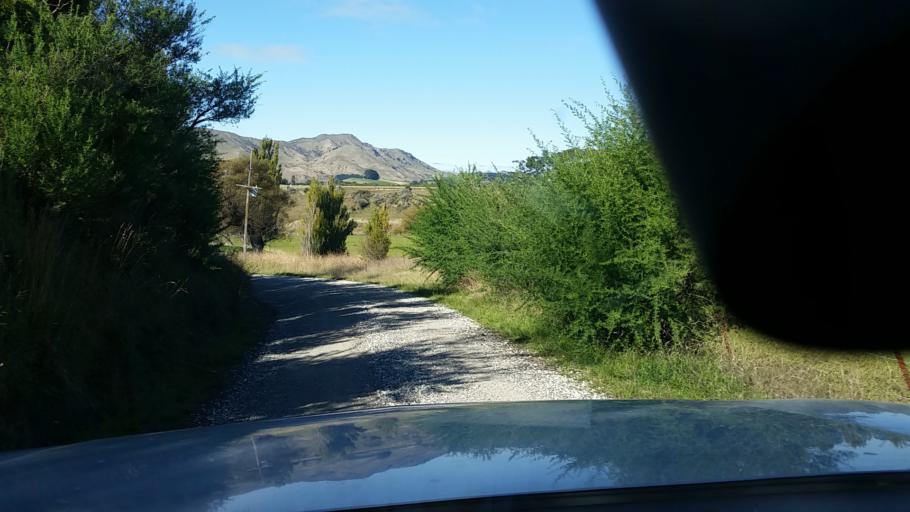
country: NZ
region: Marlborough
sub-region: Marlborough District
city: Blenheim
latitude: -41.8249
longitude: 174.1181
